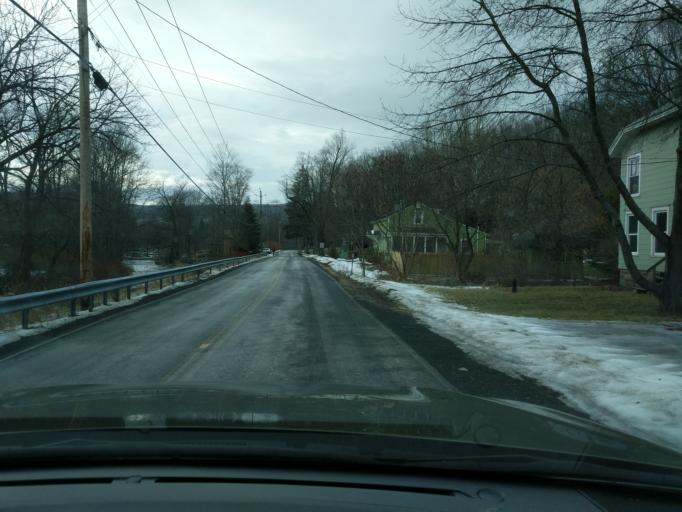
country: US
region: New York
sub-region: Tompkins County
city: East Ithaca
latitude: 42.3822
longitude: -76.3912
